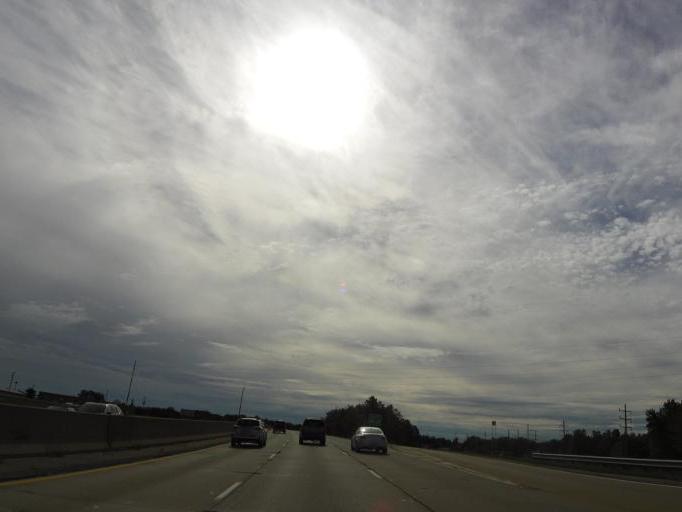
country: US
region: Ohio
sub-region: Summit County
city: Boston Heights
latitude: 41.2365
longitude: -81.4937
